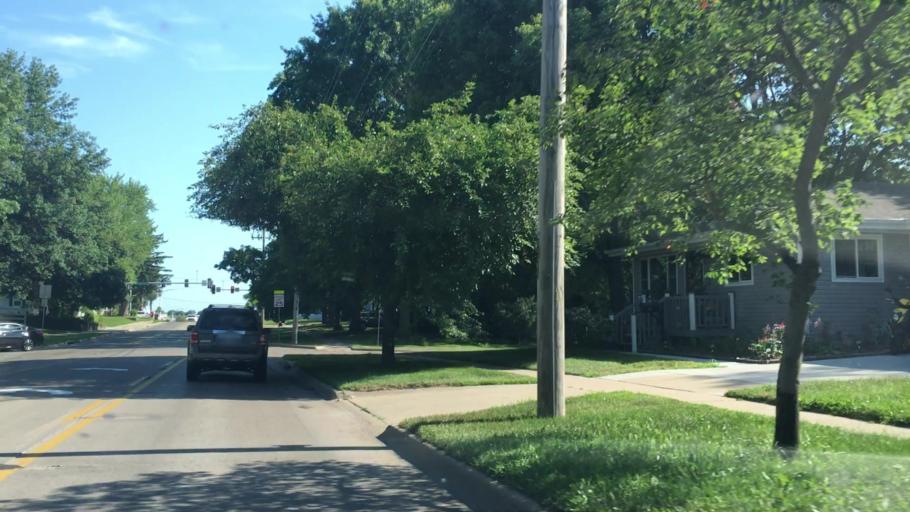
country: US
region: Iowa
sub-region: Johnson County
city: Iowa City
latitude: 41.6478
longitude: -91.5021
